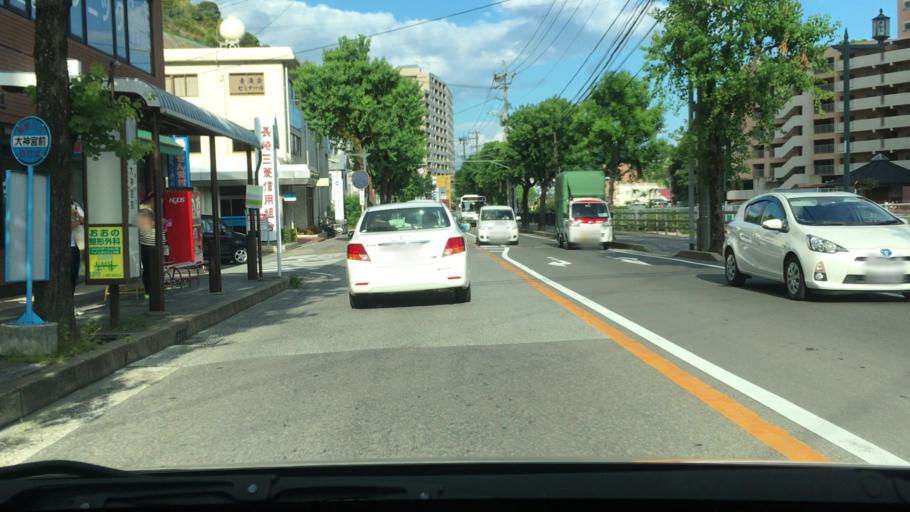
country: JP
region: Nagasaki
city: Togitsu
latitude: 32.8076
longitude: 129.8384
